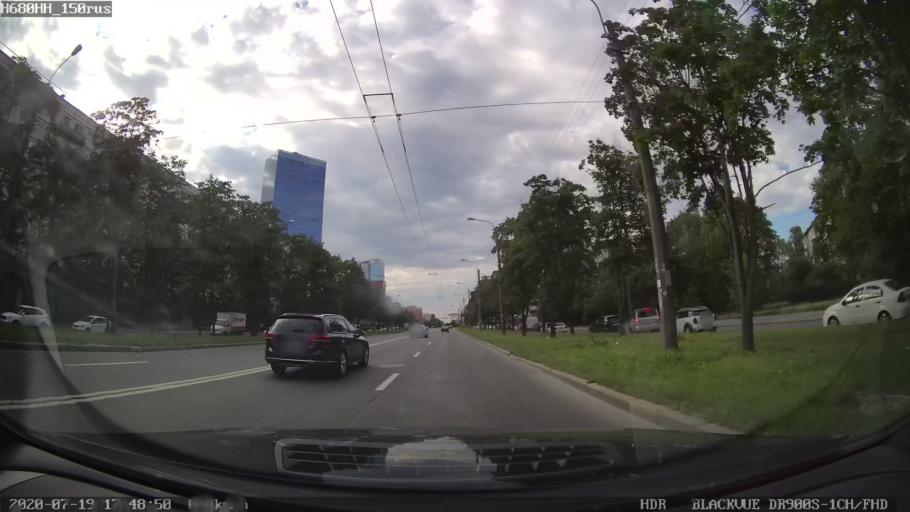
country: RU
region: St.-Petersburg
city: Kupchino
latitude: 59.8491
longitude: 30.3102
